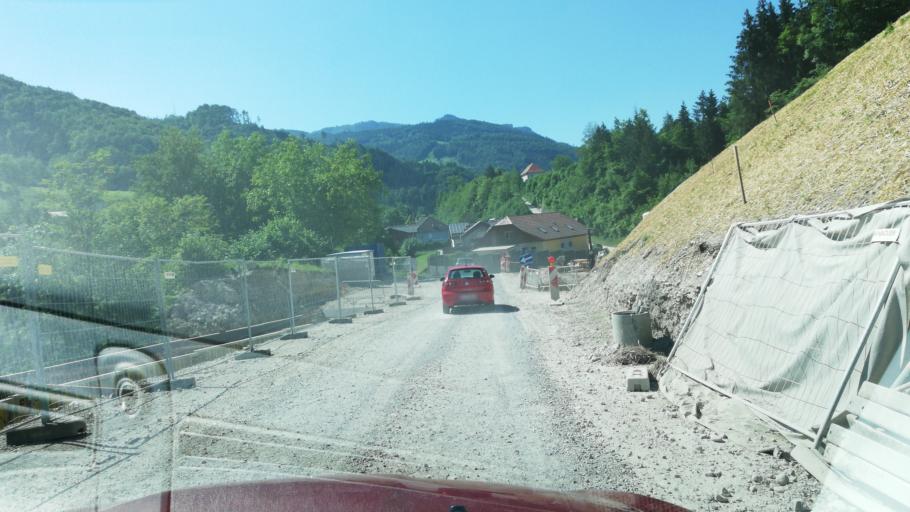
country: AT
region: Upper Austria
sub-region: Politischer Bezirk Kirchdorf an der Krems
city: Gruenburg
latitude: 47.9565
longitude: 14.2542
